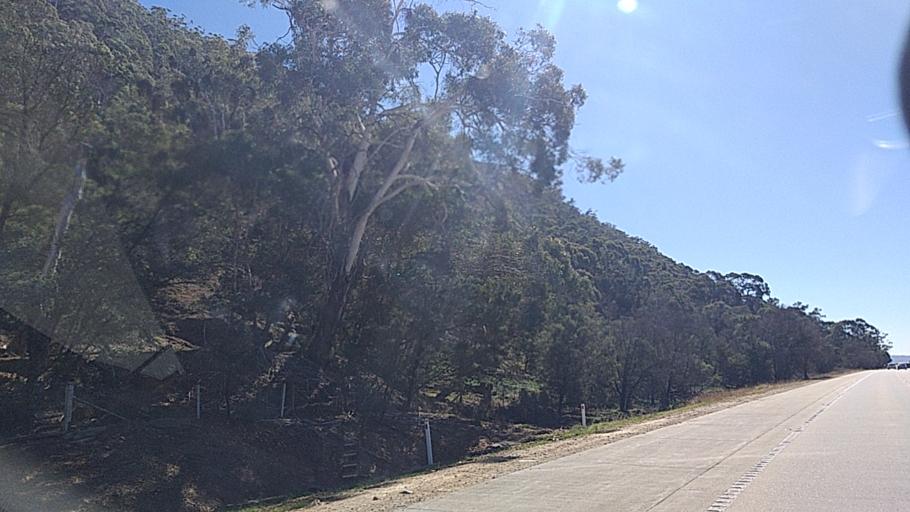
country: AU
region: New South Wales
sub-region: Yass Valley
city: Gundaroo
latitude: -35.0491
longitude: 149.3757
